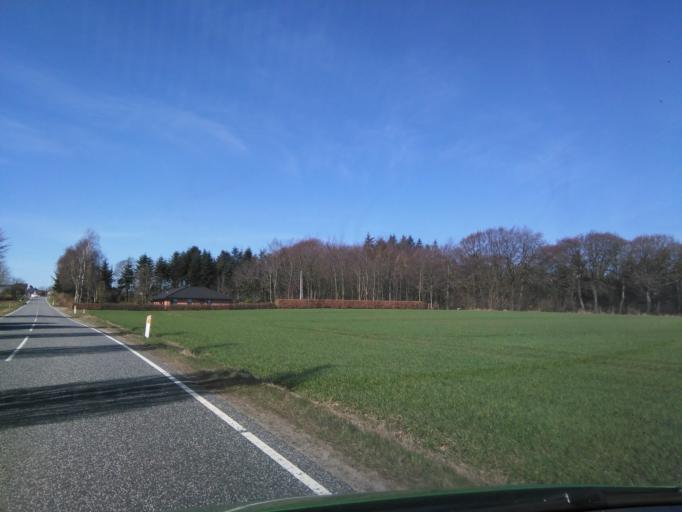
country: DK
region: Central Jutland
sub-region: Skanderborg Kommune
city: Ry
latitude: 56.0240
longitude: 9.7459
